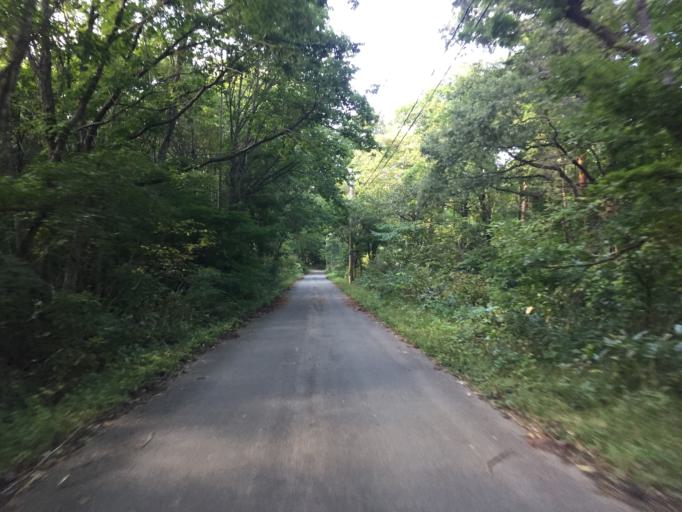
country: JP
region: Yamagata
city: Yonezawa
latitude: 37.8304
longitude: 140.2114
